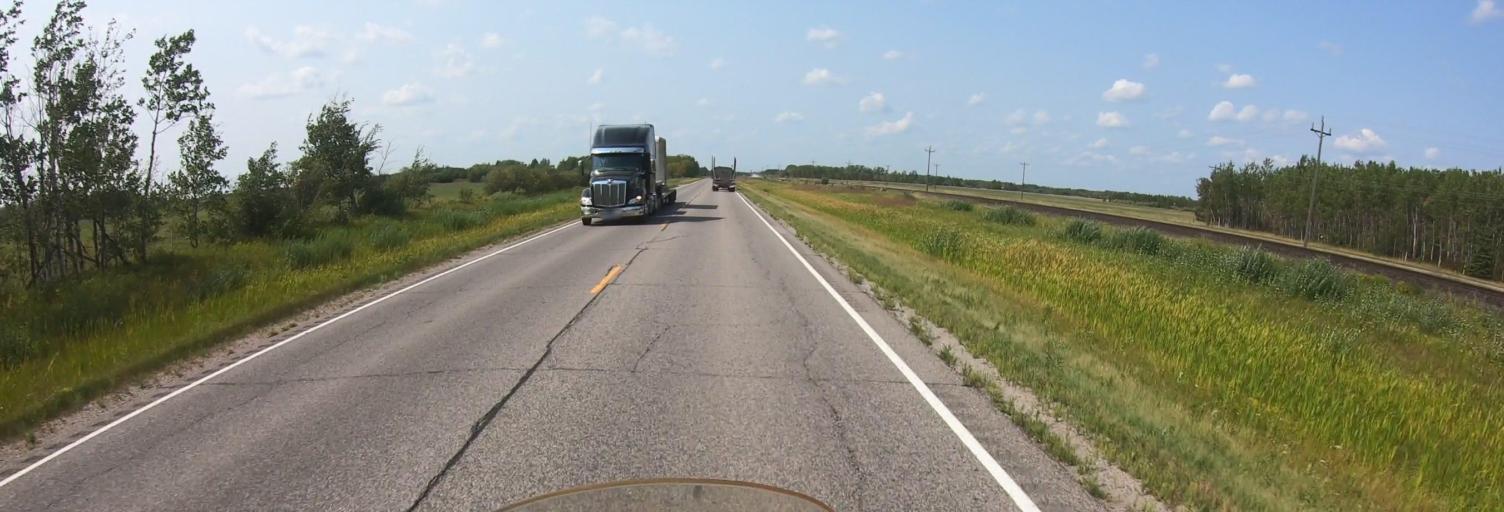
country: US
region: Minnesota
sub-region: Roseau County
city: Warroad
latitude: 48.8669
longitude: -95.2555
